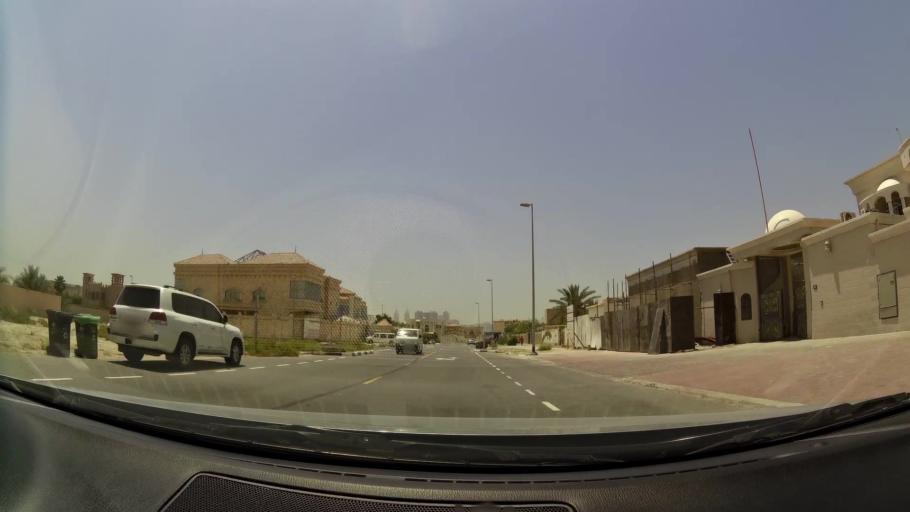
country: AE
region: Dubai
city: Dubai
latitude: 25.0877
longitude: 55.2011
